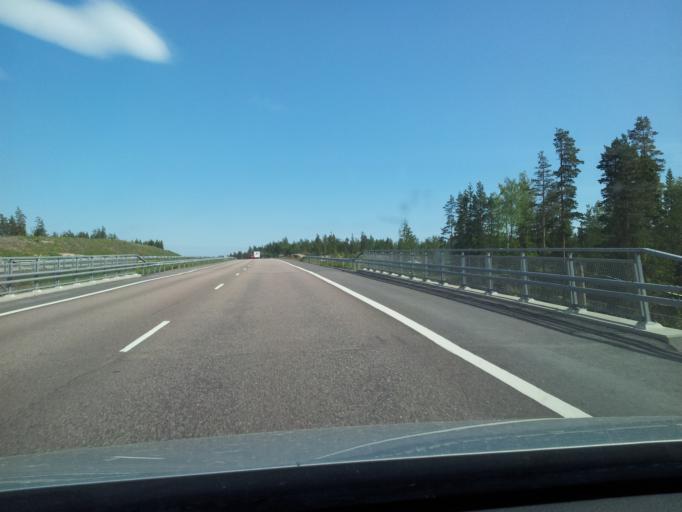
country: FI
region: Uusimaa
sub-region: Loviisa
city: Perna
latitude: 60.4829
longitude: 26.0228
